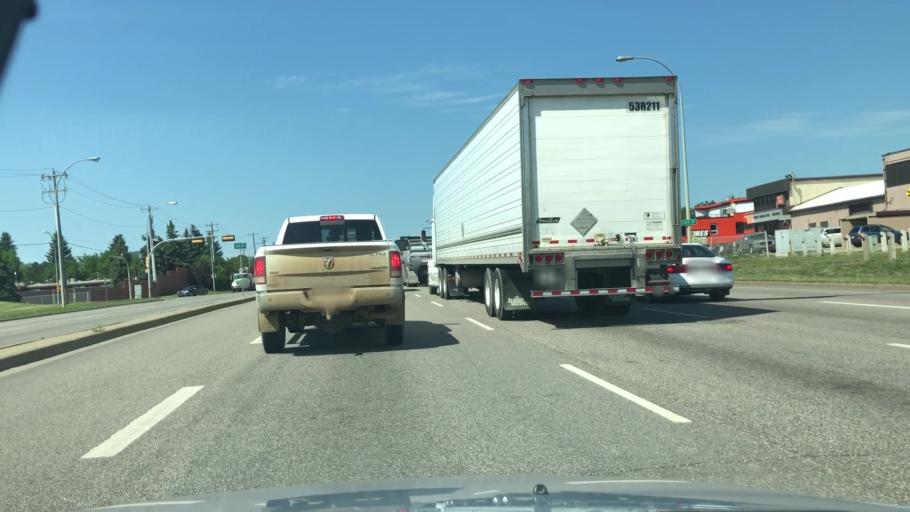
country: CA
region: Alberta
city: Edmonton
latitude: 53.5806
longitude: -113.5342
